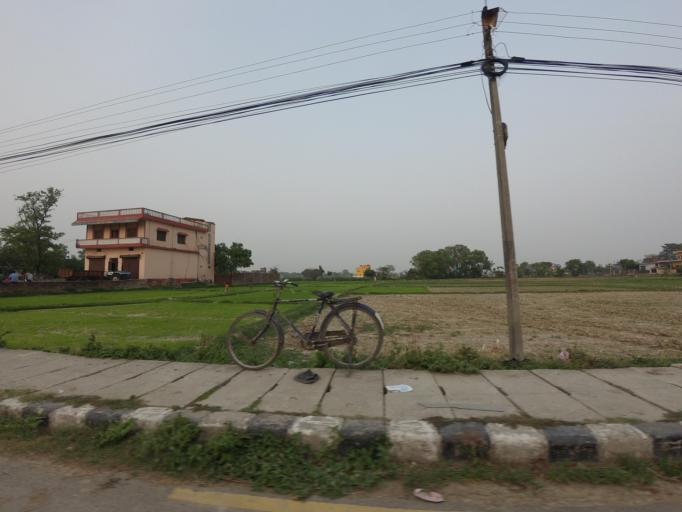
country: NP
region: Western Region
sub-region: Lumbini Zone
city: Bhairahawa
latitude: 27.5149
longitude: 83.4642
